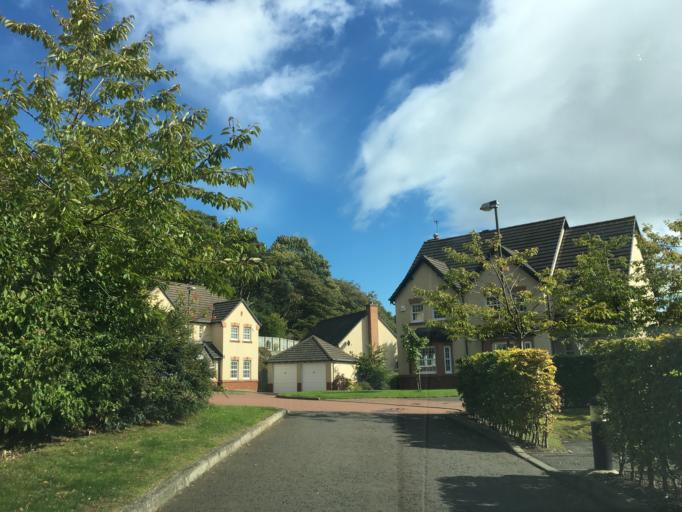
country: GB
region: Scotland
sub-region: Midlothian
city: Loanhead
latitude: 55.9011
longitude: -3.1972
